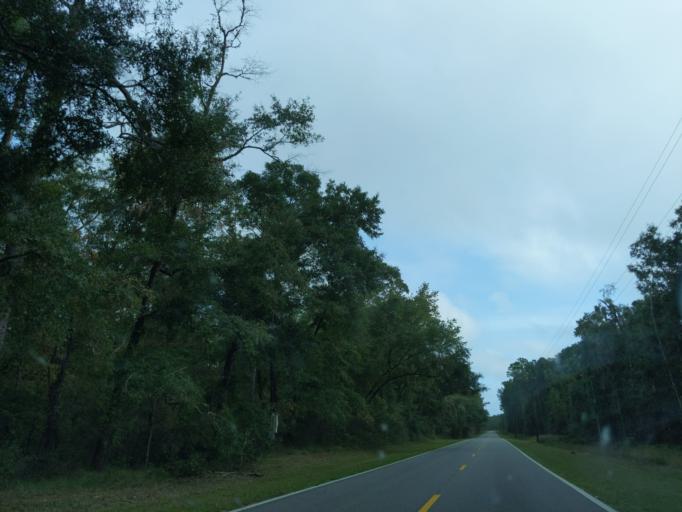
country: US
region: Florida
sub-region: Wakulla County
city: Crawfordville
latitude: 30.1177
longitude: -84.3133
